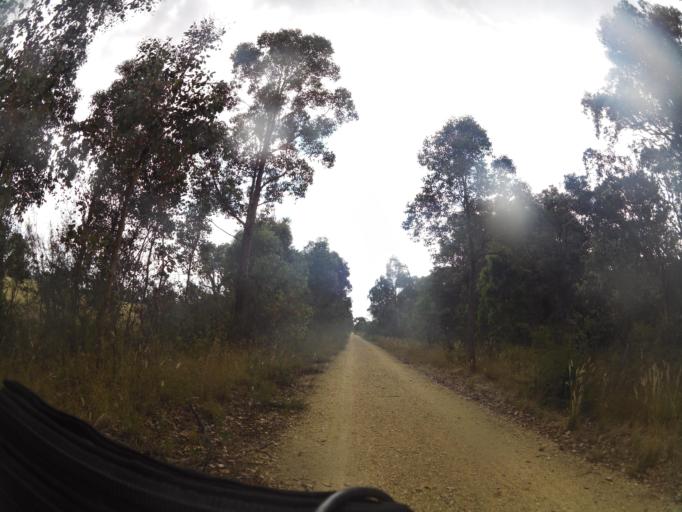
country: AU
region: Victoria
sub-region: Wellington
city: Heyfield
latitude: -38.0346
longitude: 146.6561
